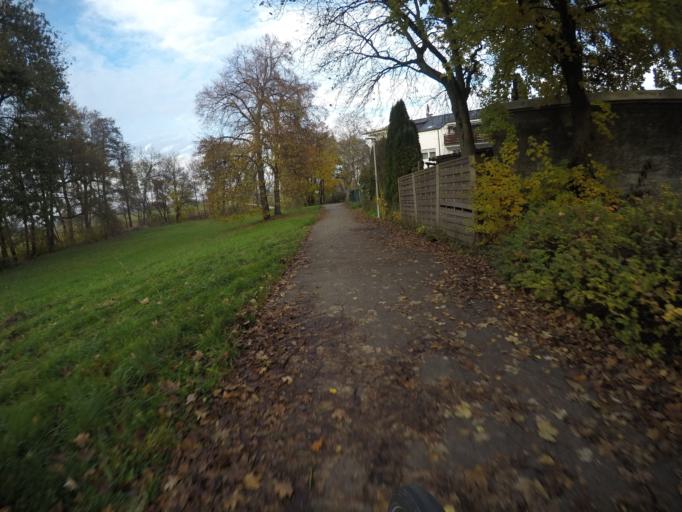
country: DE
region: Baden-Wuerttemberg
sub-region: Regierungsbezirk Stuttgart
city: Leinfelden-Echterdingen
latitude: 48.7107
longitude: 9.1457
